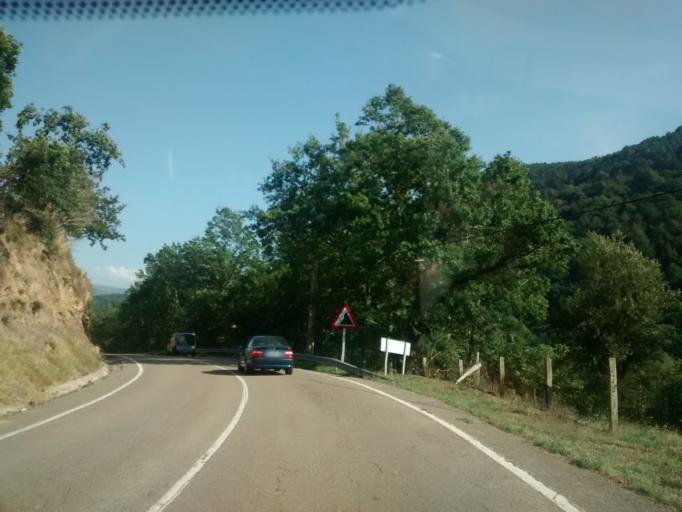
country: ES
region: Cantabria
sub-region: Provincia de Cantabria
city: Ruente
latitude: 43.1664
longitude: -4.2702
